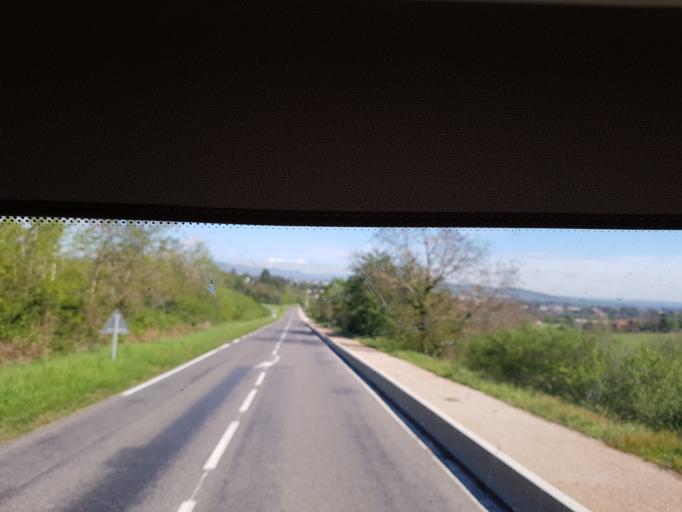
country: FR
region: Rhone-Alpes
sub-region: Departement du Rhone
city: Lentilly
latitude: 45.8089
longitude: 4.6644
